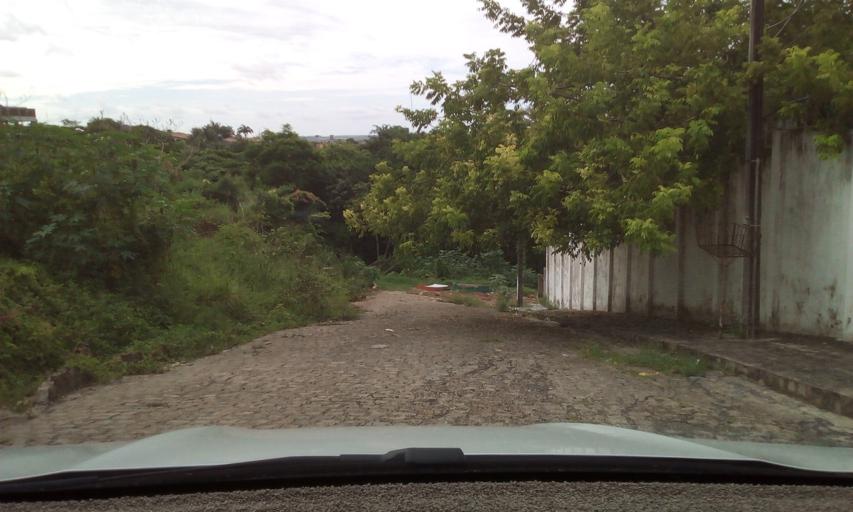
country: BR
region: Paraiba
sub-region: Joao Pessoa
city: Joao Pessoa
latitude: -7.1059
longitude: -34.8540
